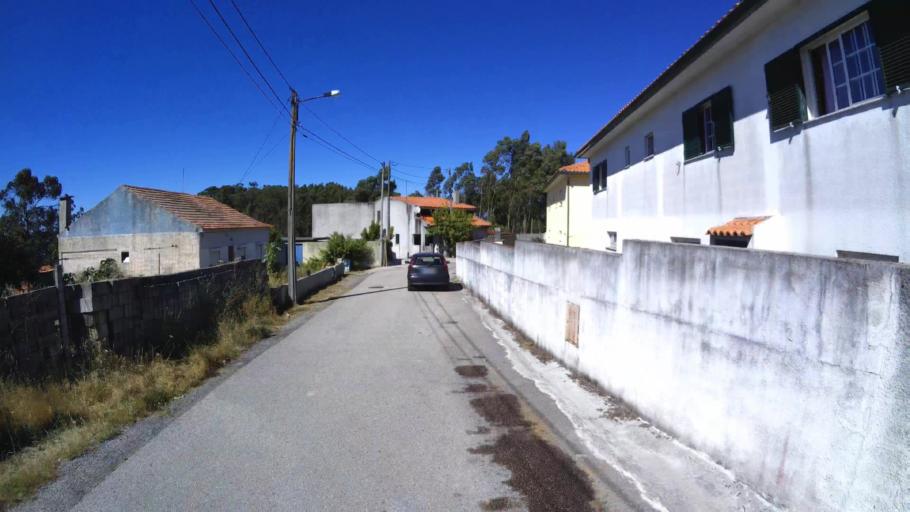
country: PT
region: Aveiro
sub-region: Aveiro
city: Aveiro
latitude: 40.6638
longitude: -8.6229
